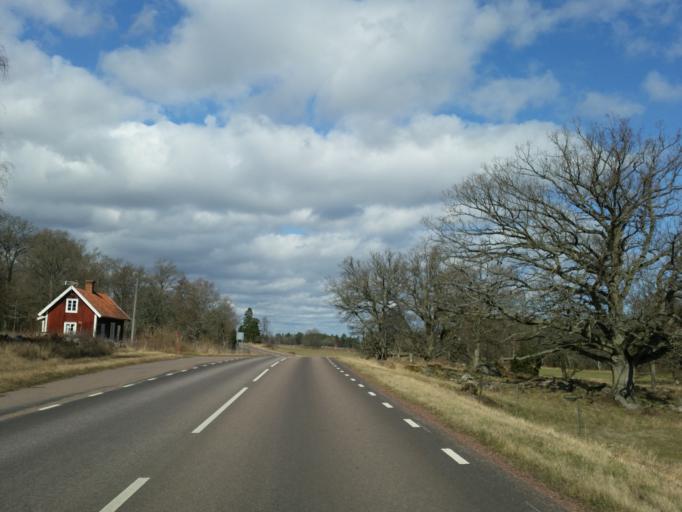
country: SE
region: Kalmar
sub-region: Monsteras Kommun
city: Timmernabben
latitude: 56.9204
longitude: 16.4226
